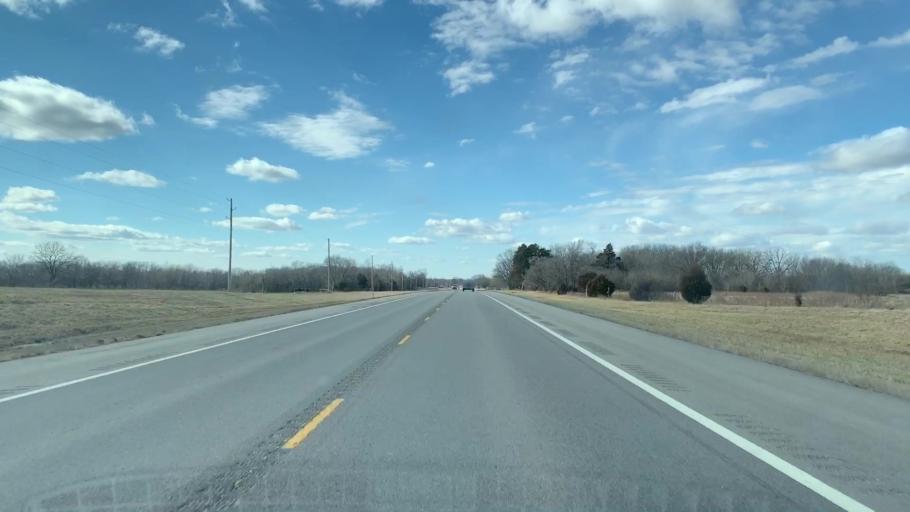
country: US
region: Kansas
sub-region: Labette County
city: Oswego
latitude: 37.3401
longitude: -95.0579
